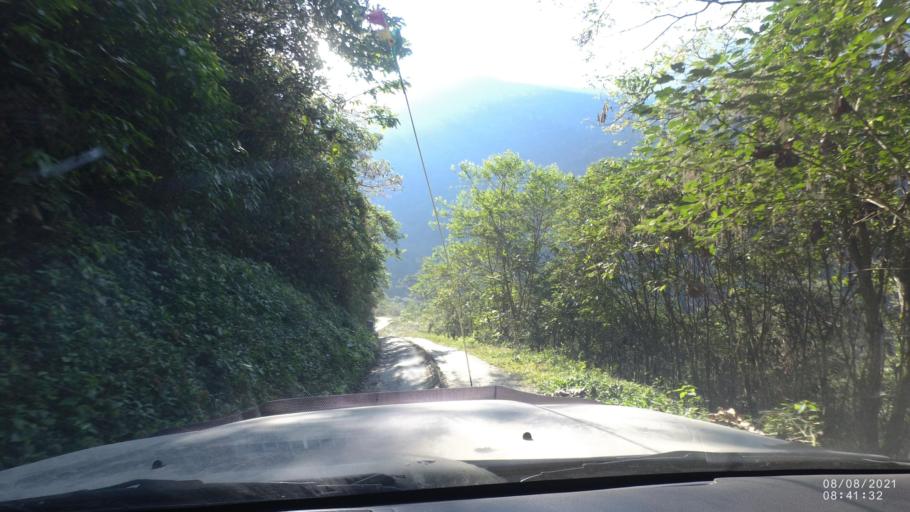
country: BO
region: La Paz
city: Quime
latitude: -16.5268
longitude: -66.7575
